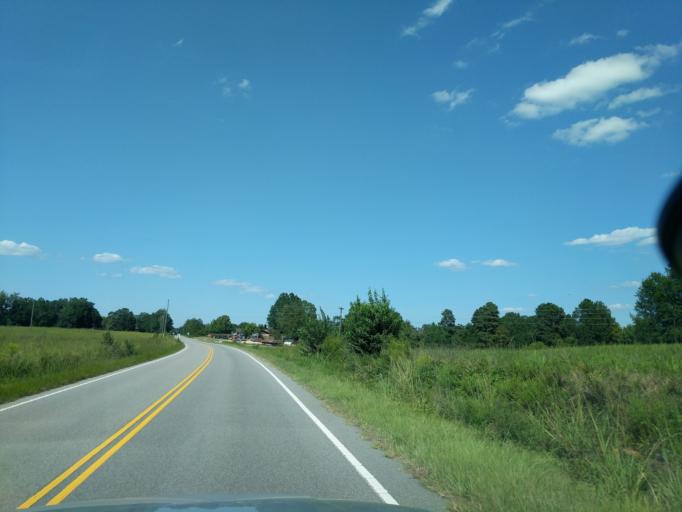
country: US
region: South Carolina
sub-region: Newberry County
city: Prosperity
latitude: 34.1290
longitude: -81.5422
